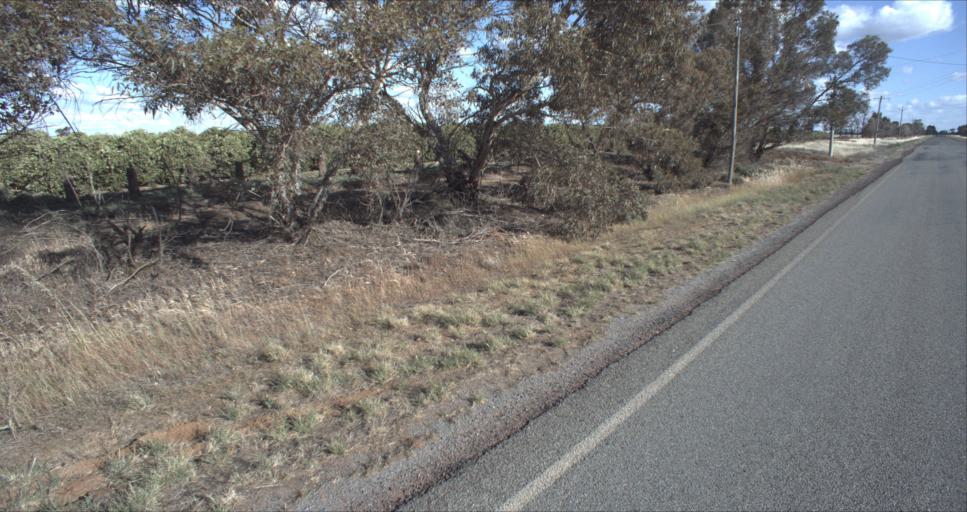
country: AU
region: New South Wales
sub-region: Leeton
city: Leeton
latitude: -34.5273
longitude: 146.2821
